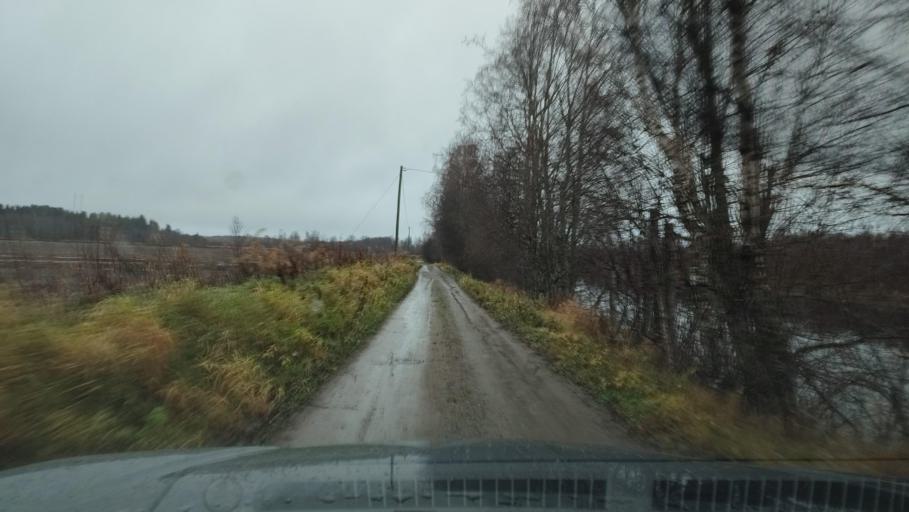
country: FI
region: Ostrobothnia
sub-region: Sydosterbotten
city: Kristinestad
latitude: 62.2309
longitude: 21.4505
